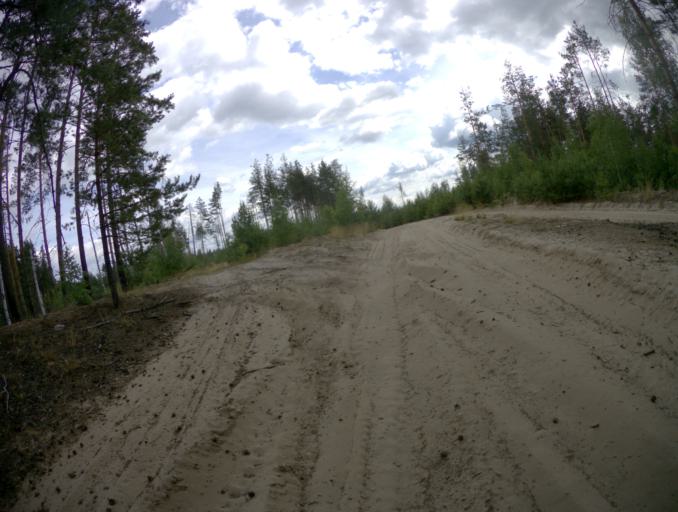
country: RU
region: Nizjnij Novgorod
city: Frolishchi
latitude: 56.4871
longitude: 42.5755
